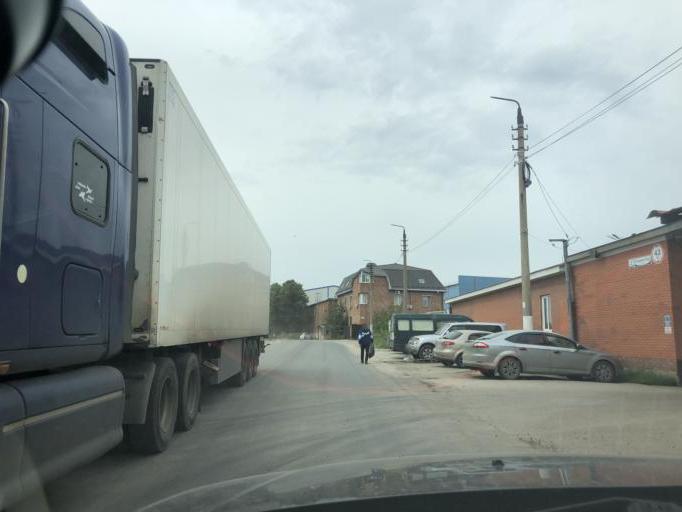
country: RU
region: Tula
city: Tula
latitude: 54.2190
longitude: 37.6738
